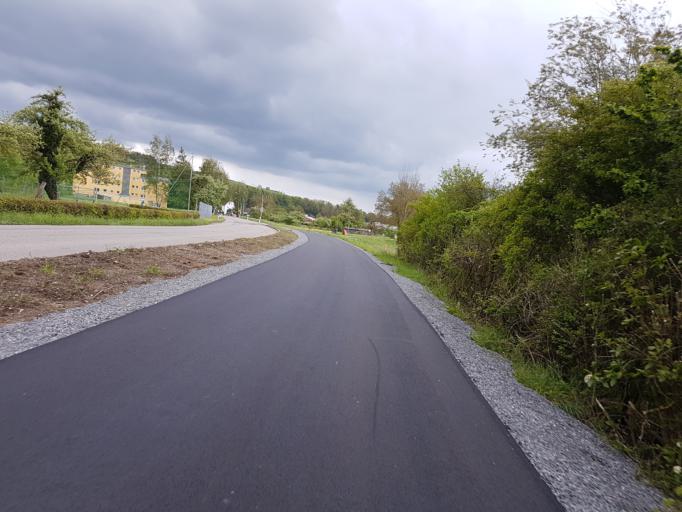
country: DE
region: Baden-Wuerttemberg
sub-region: Freiburg Region
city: Wutoschingen
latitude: 47.6733
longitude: 8.3784
